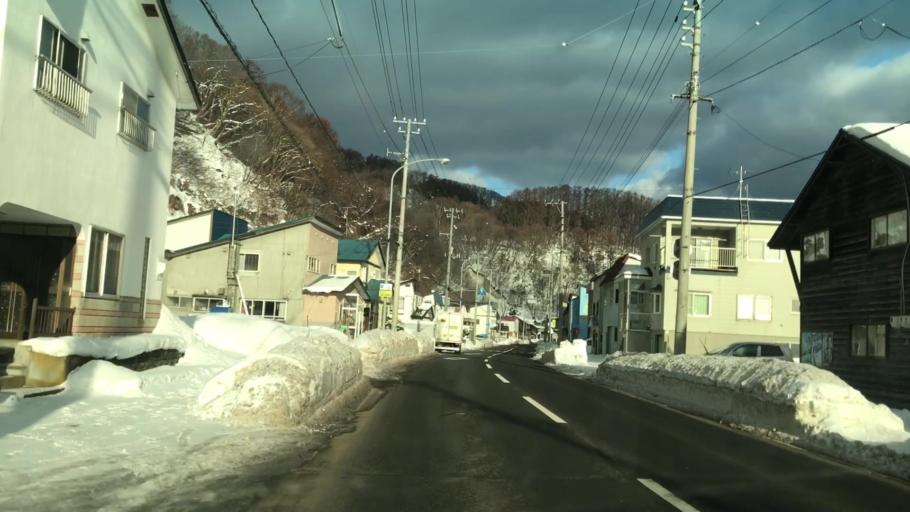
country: JP
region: Hokkaido
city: Yoichi
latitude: 43.2719
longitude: 140.6363
